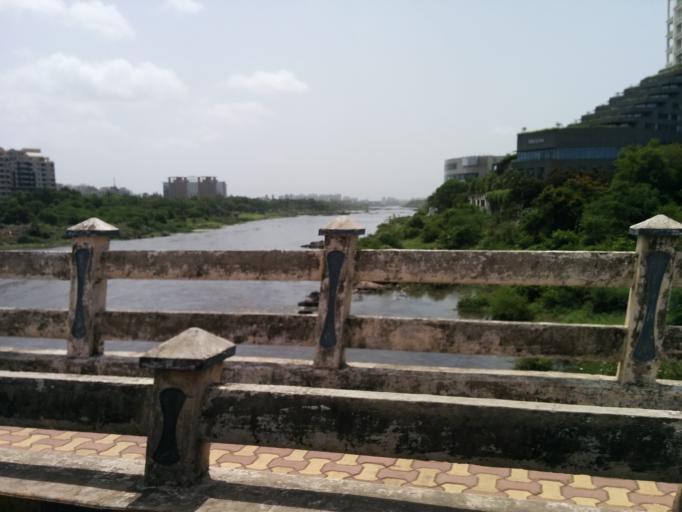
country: IN
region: Maharashtra
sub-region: Pune Division
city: Shivaji Nagar
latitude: 18.5409
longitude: 73.9042
